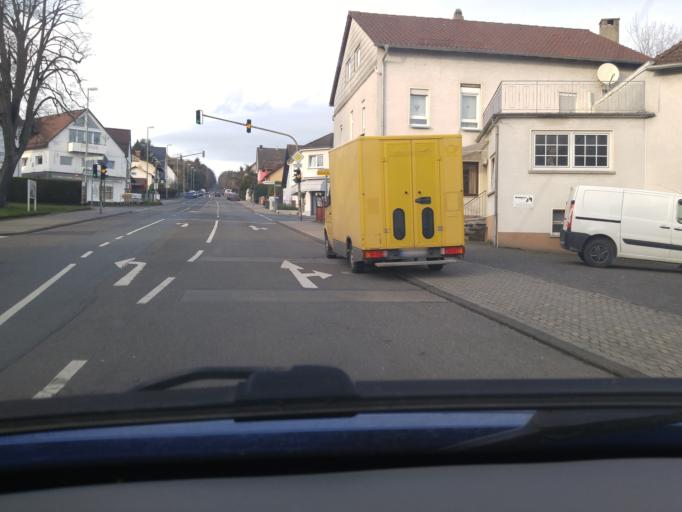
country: DE
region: Hesse
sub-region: Regierungsbezirk Darmstadt
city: Bad Soden am Taunus
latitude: 50.1562
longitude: 8.4900
